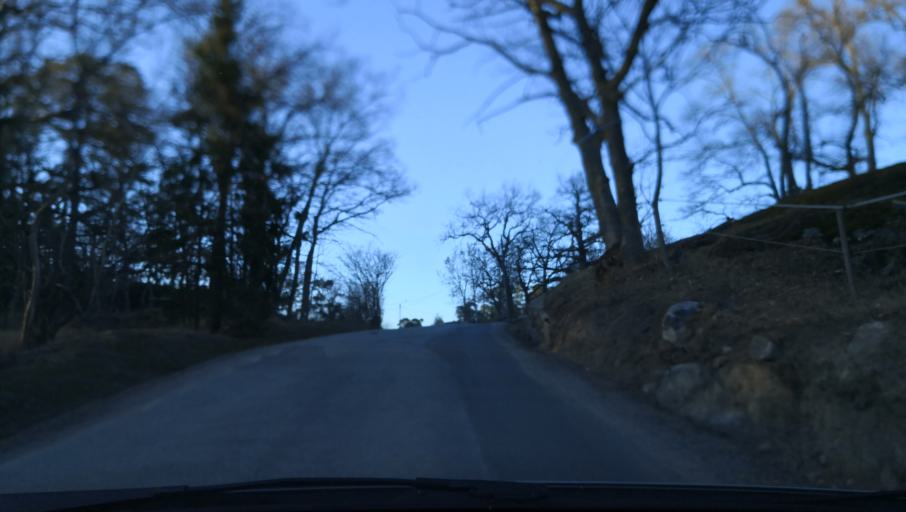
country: SE
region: Stockholm
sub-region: Varmdo Kommun
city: Mortnas
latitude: 59.3349
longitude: 18.4401
